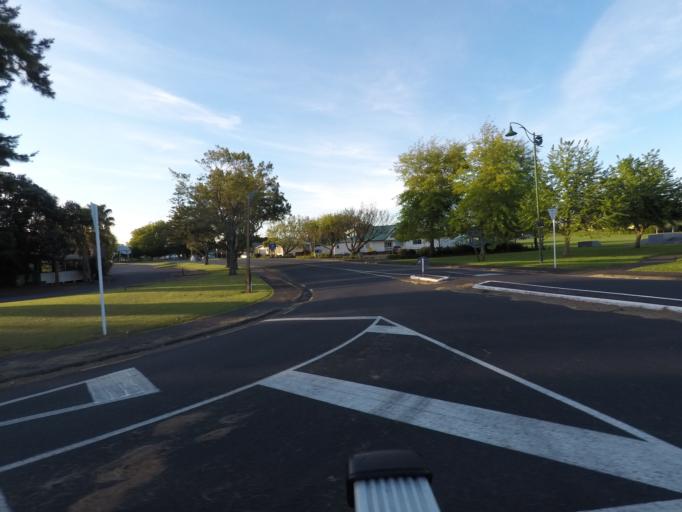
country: NZ
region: Auckland
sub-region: Auckland
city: Rosebank
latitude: -36.8424
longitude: 174.6540
